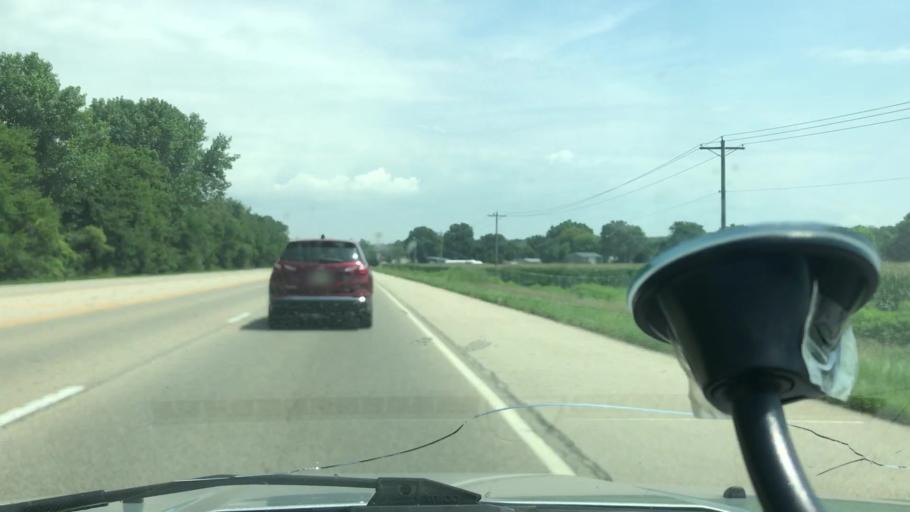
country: US
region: Illinois
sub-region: Tazewell County
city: North Pekin
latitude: 40.6142
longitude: -89.6303
